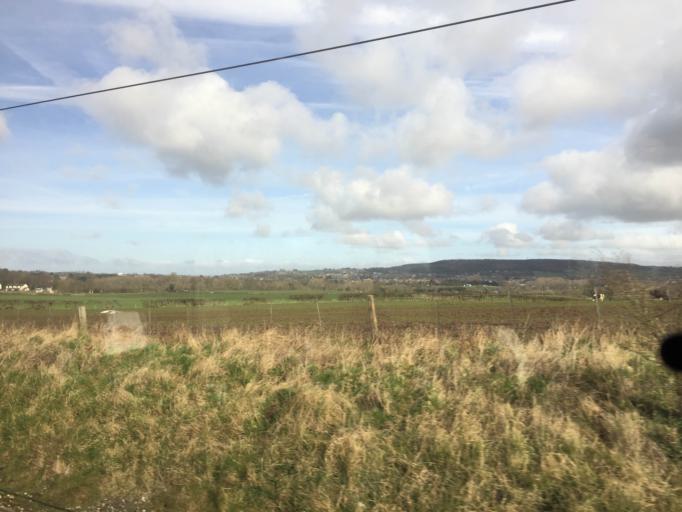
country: GB
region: England
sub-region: Cumbria
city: Penrith
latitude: 54.6385
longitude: -2.7505
